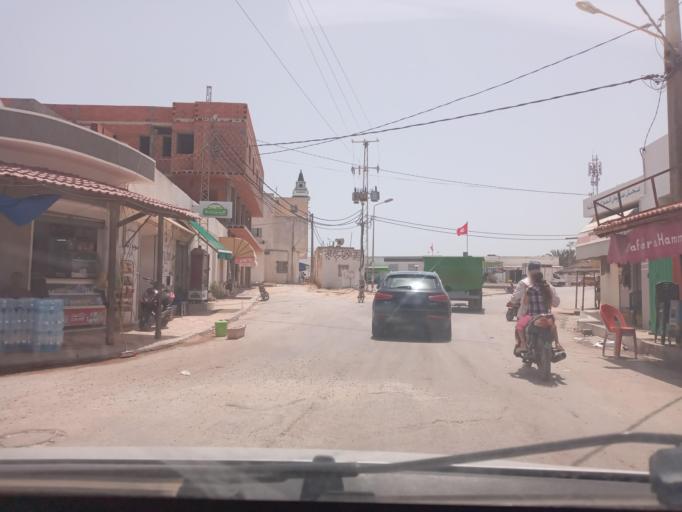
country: TN
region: Nabul
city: El Haouaria
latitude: 37.0121
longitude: 10.9534
